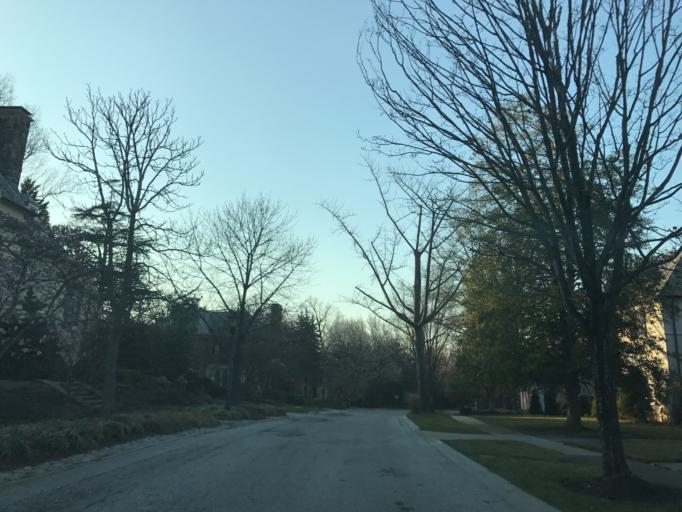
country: US
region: Maryland
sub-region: City of Baltimore
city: Baltimore
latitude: 39.3403
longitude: -76.6114
